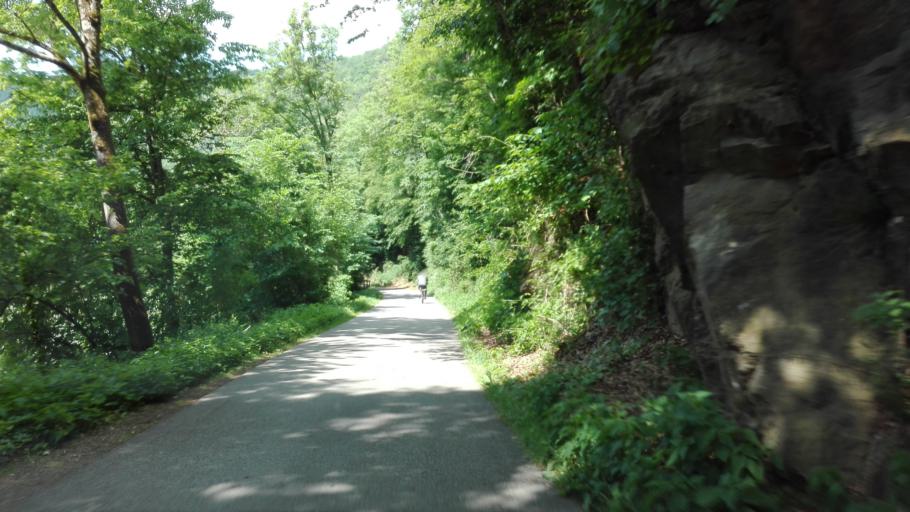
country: AT
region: Upper Austria
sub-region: Politischer Bezirk Rohrbach
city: Atzesberg
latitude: 48.4276
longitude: 13.8764
